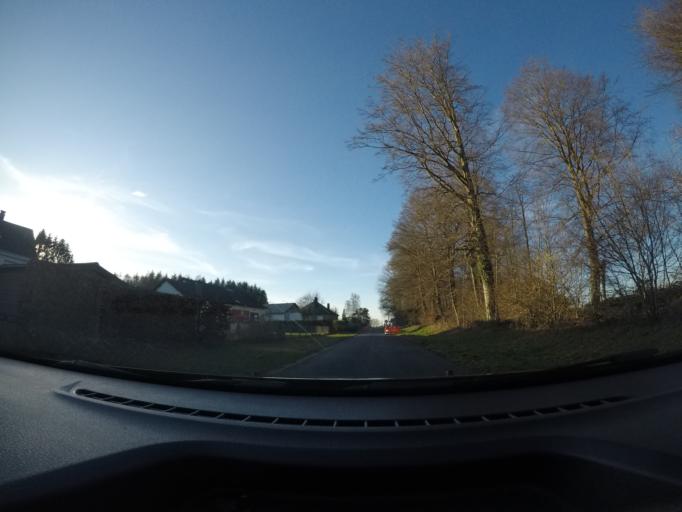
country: BE
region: Wallonia
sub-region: Province du Luxembourg
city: Tintigny
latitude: 49.6758
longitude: 5.4848
